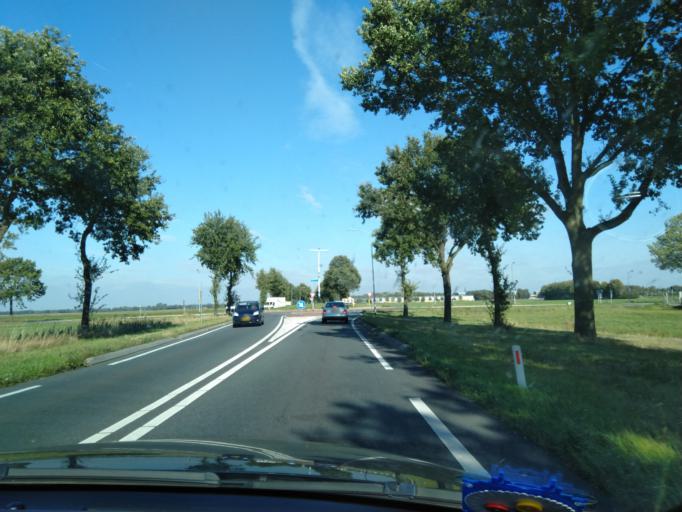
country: NL
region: Groningen
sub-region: Gemeente Pekela
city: Oude Pekela
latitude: 53.0882
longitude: 6.9697
